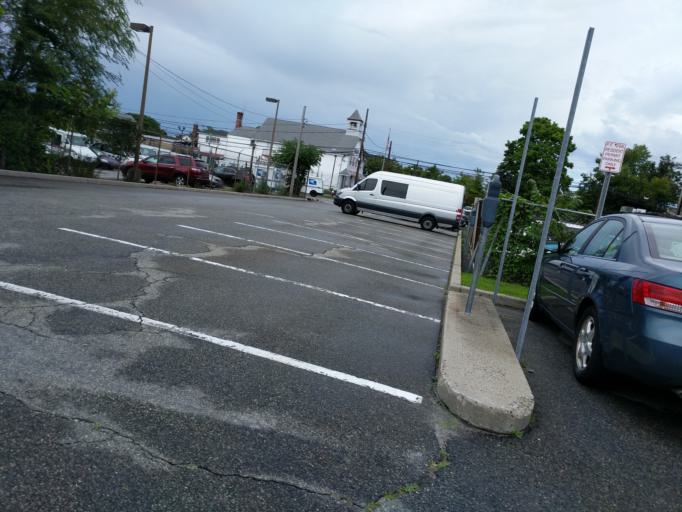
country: US
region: New York
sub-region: Nassau County
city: Valley Stream
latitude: 40.6609
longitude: -73.7016
